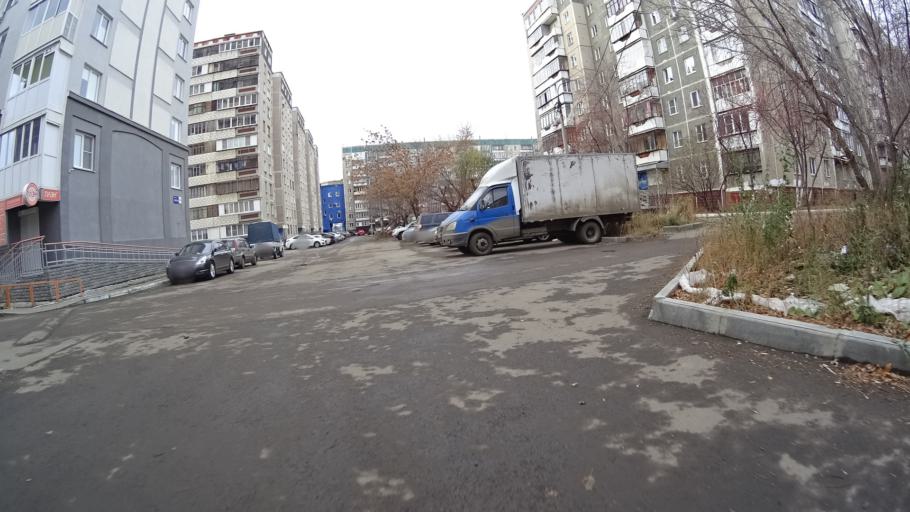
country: RU
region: Chelyabinsk
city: Roshchino
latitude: 55.1853
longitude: 61.2954
